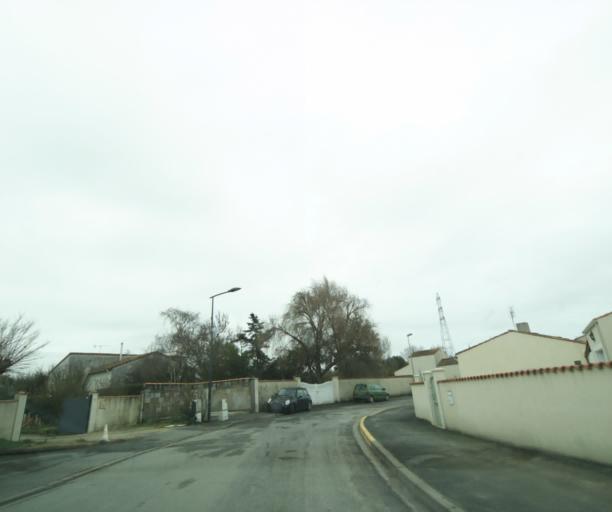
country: FR
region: Poitou-Charentes
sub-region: Departement de la Charente-Maritime
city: Lagord
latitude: 46.1839
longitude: -1.1398
